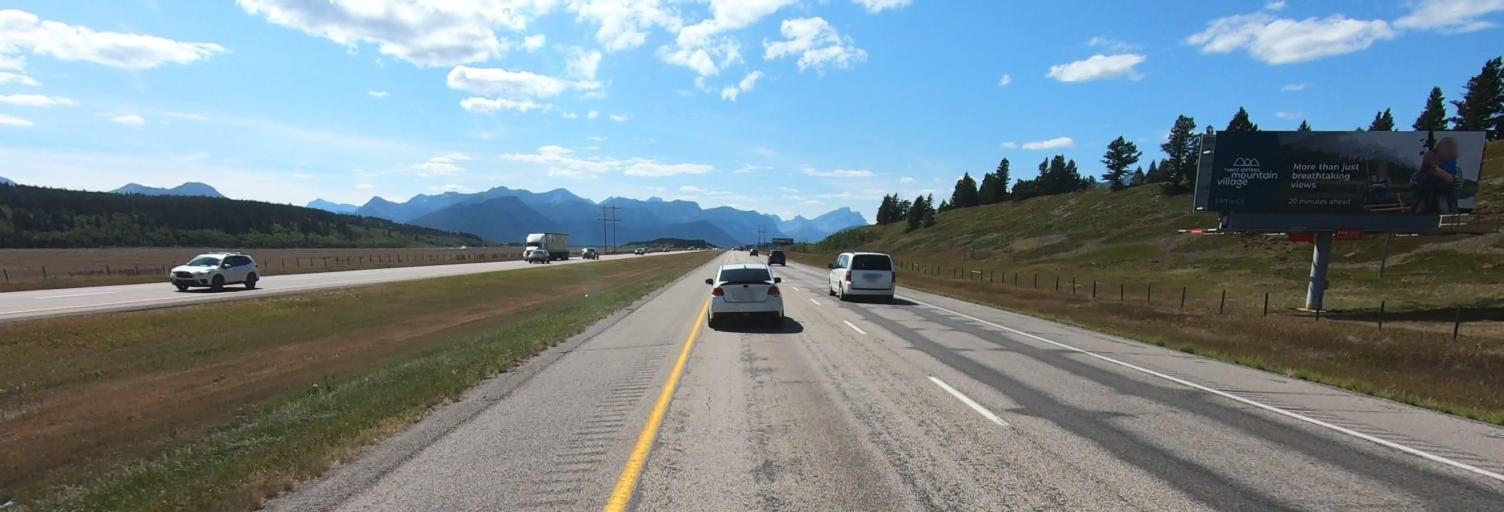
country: CA
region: Alberta
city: Canmore
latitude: 51.1251
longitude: -114.9637
